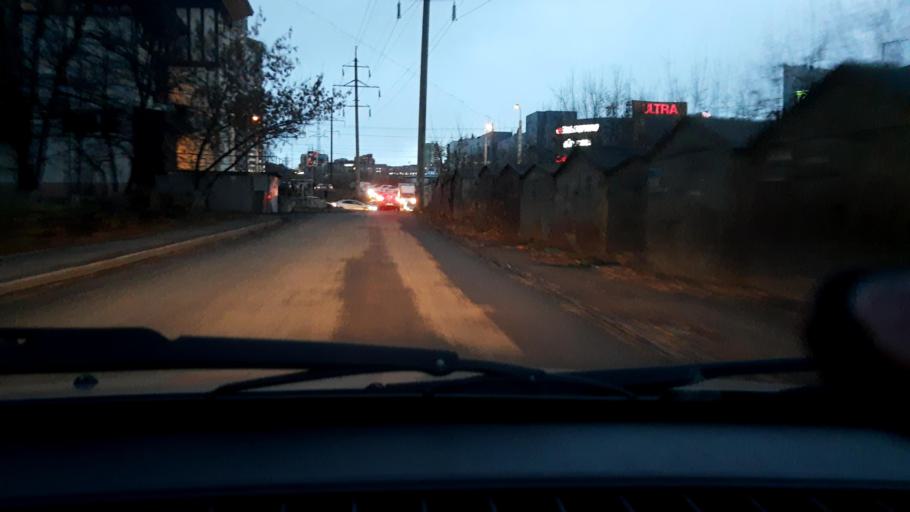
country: RU
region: Bashkortostan
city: Ufa
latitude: 54.7200
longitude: 55.9852
